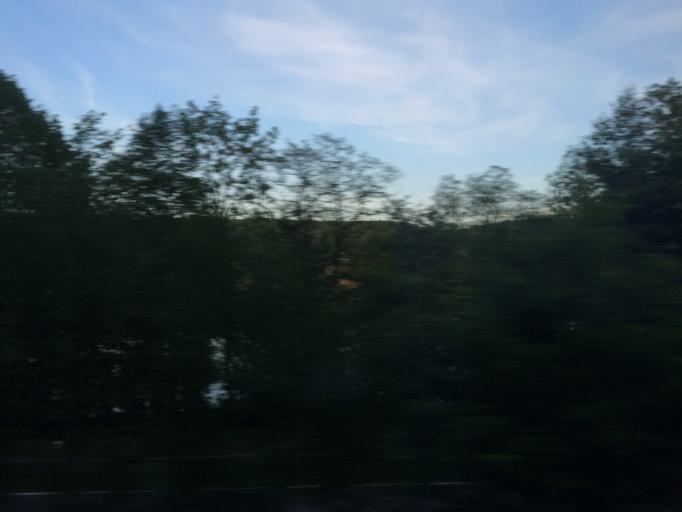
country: DE
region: Bavaria
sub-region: Regierungsbezirk Unterfranken
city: Lohr am Main
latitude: 50.0149
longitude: 9.6073
